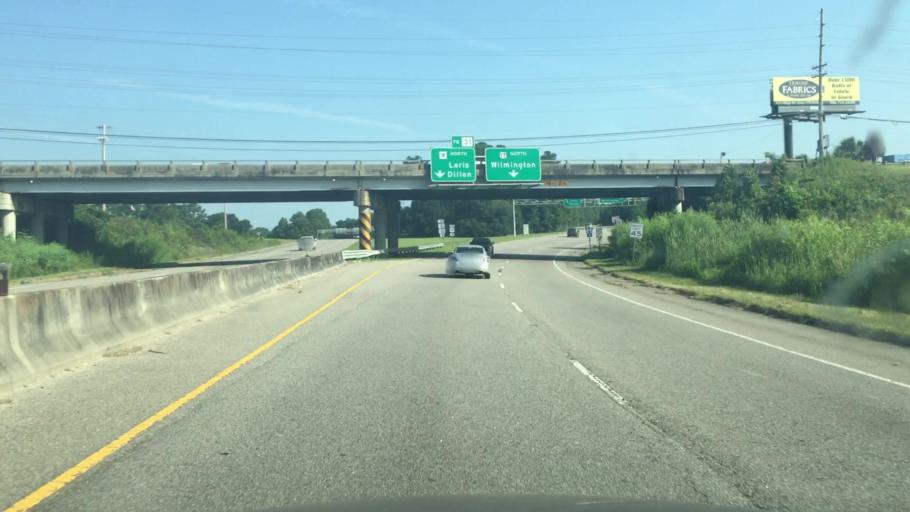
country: US
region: South Carolina
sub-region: Horry County
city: Little River
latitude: 33.8586
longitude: -78.6564
